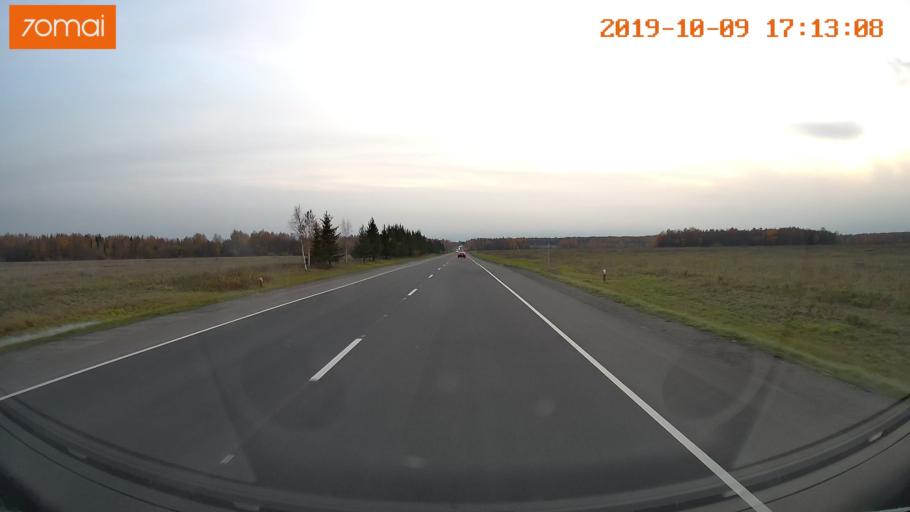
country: RU
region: Ivanovo
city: Privolzhsk
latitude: 57.3189
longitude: 41.2292
